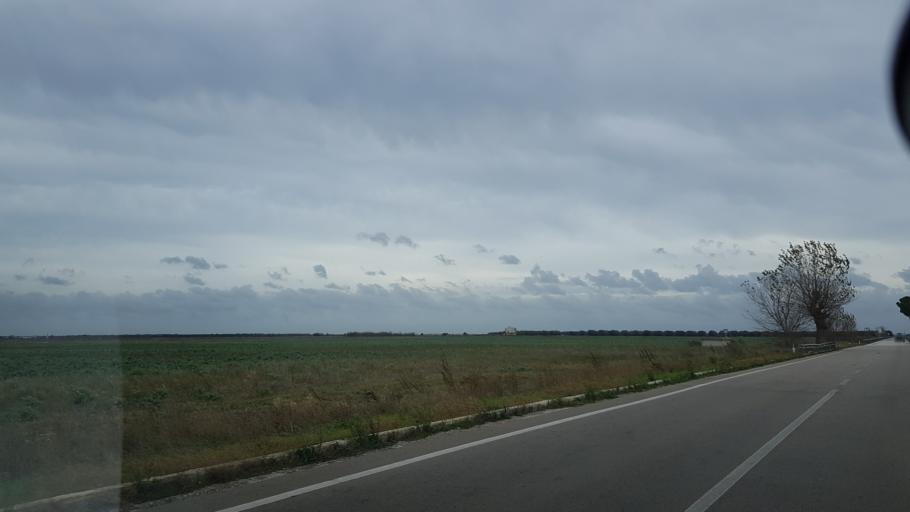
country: IT
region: Apulia
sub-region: Provincia di Brindisi
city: San Pancrazio Salentino
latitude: 40.4110
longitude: 17.8688
